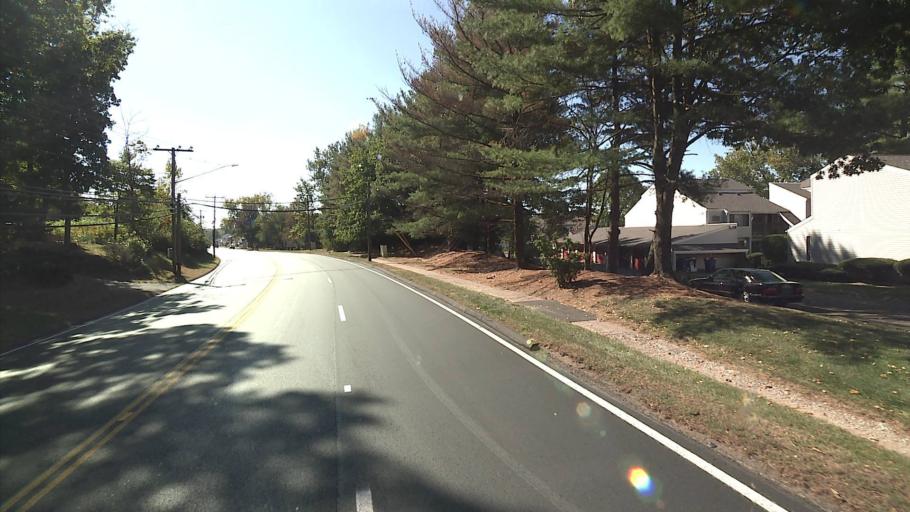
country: US
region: Connecticut
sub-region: Tolland County
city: Rockville
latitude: 41.8583
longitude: -72.4850
